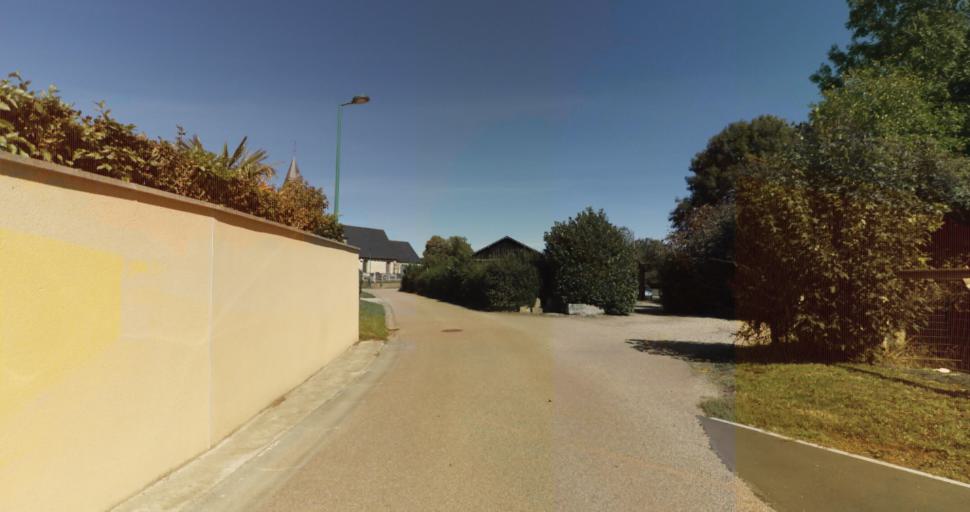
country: FR
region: Lower Normandy
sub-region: Departement de l'Orne
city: Gace
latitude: 48.7674
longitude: 0.2625
